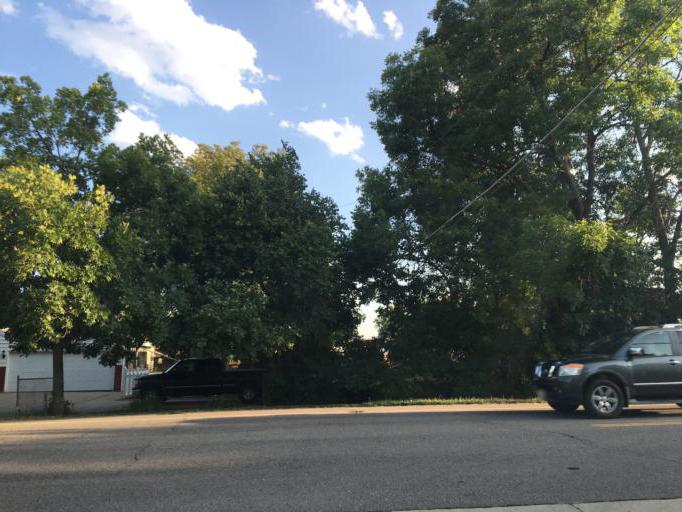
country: US
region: Colorado
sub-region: Jefferson County
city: Applewood
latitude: 39.7910
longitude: -105.1473
